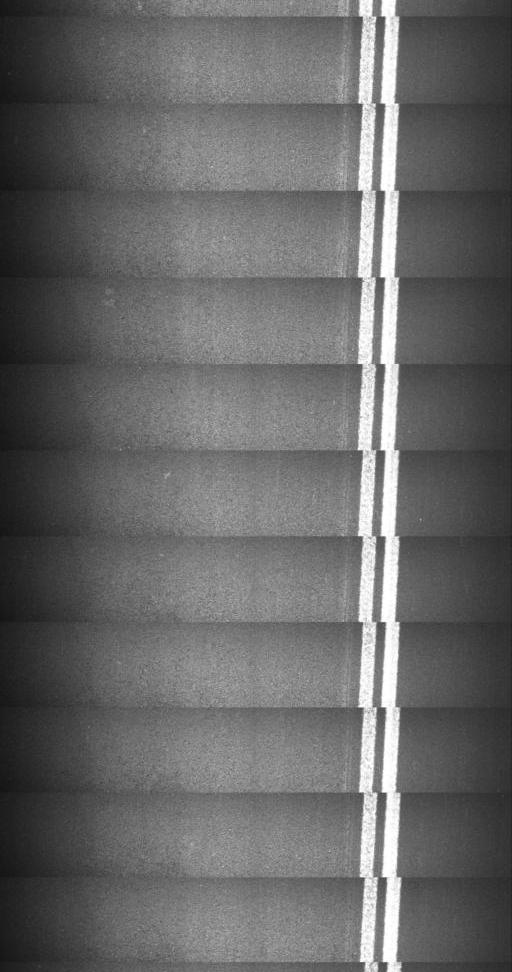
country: US
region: New Hampshire
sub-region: Grafton County
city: North Haverhill
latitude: 44.0712
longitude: -72.0564
